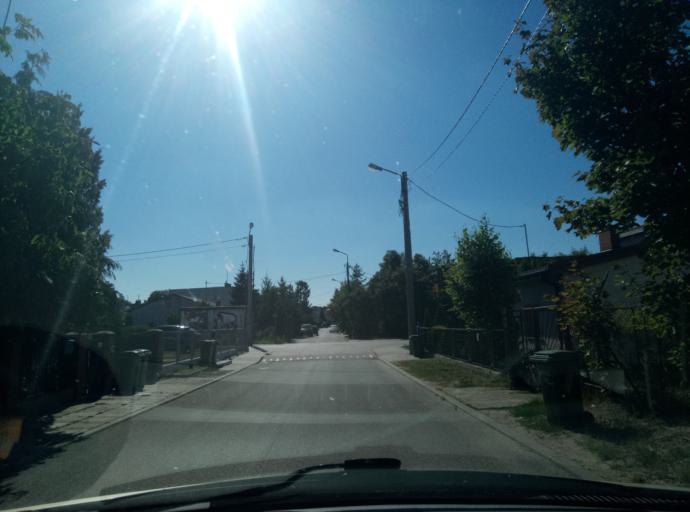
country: PL
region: Kujawsko-Pomorskie
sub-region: Torun
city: Torun
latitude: 53.0489
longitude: 18.5799
